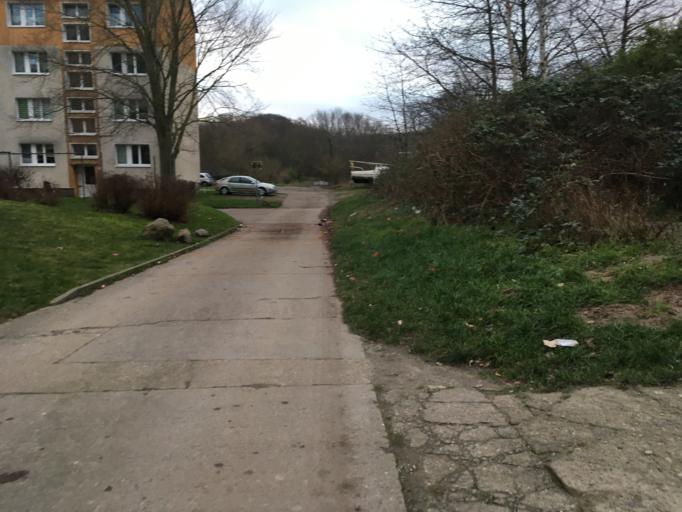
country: DE
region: Mecklenburg-Vorpommern
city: Sassnitz
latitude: 54.5110
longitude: 13.6223
